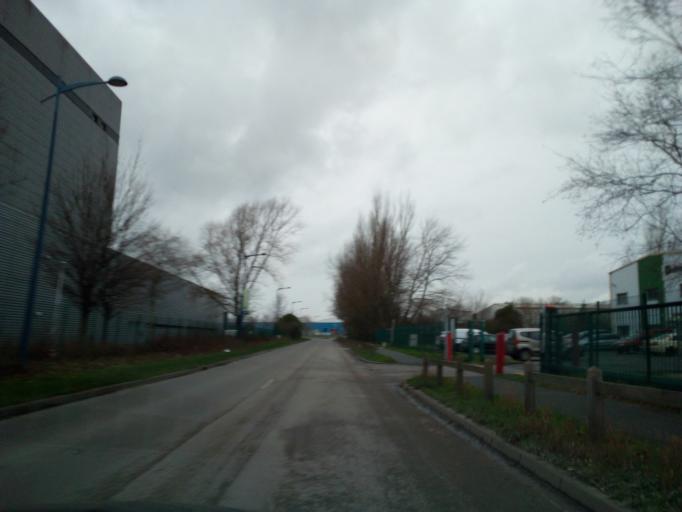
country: FR
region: Nord-Pas-de-Calais
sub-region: Departement du Pas-de-Calais
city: Billy-Berclau
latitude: 50.5235
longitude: 2.8561
